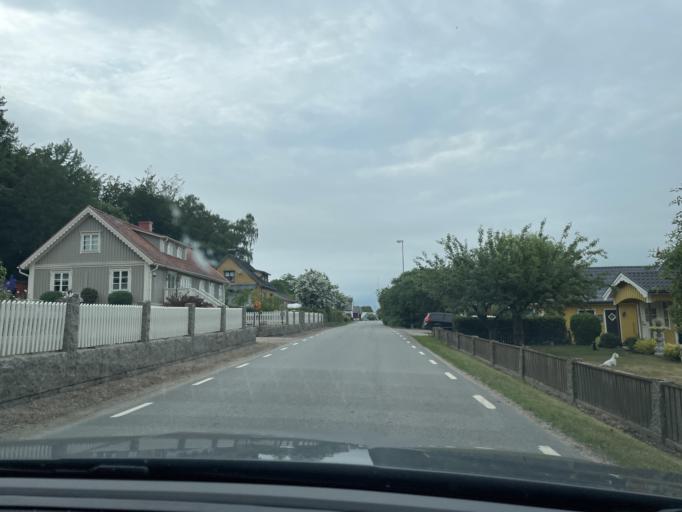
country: SE
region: Blekinge
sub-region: Solvesborgs Kommun
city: Soelvesborg
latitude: 56.0350
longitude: 14.6361
